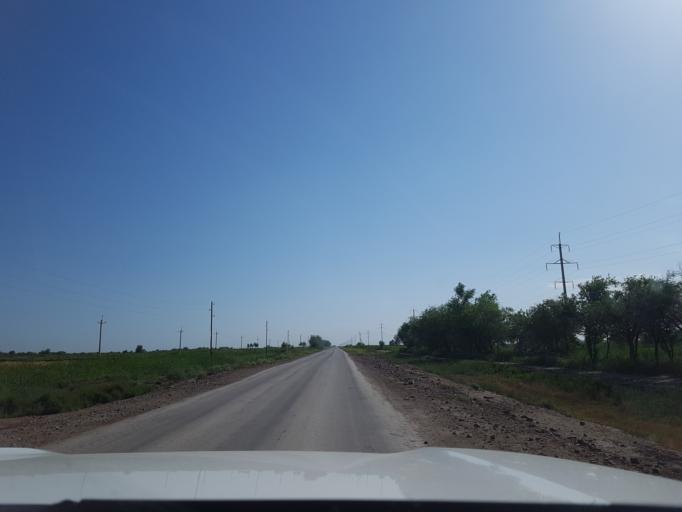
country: TM
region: Dasoguz
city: Koeneuergench
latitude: 42.1016
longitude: 58.9039
